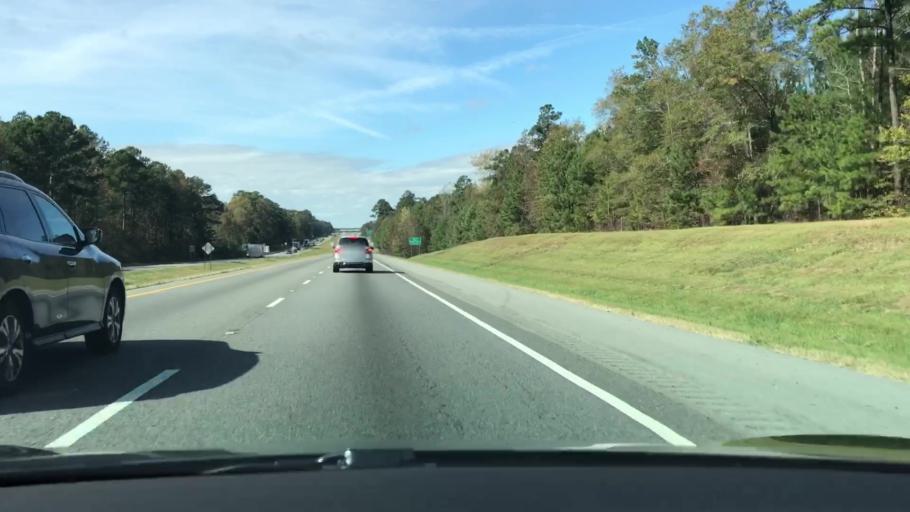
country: US
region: Georgia
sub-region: Walton County
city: Social Circle
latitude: 33.6051
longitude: -83.6727
